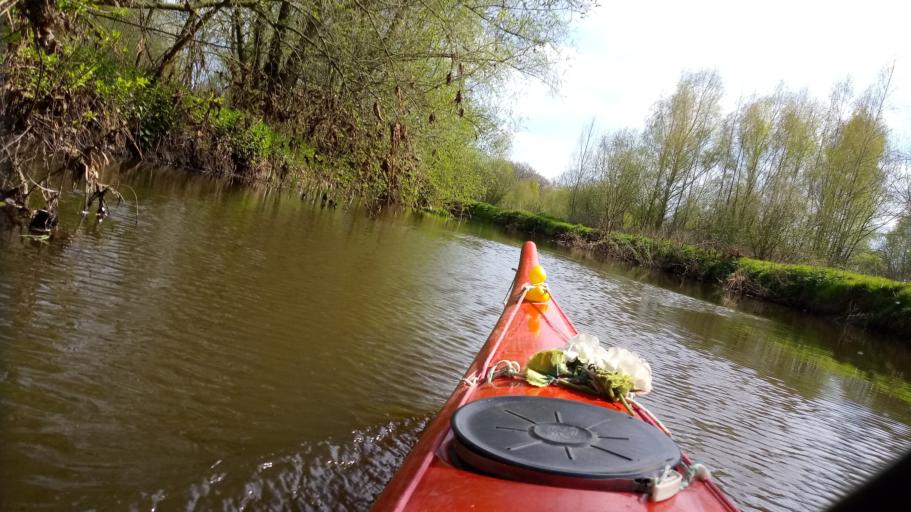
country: NL
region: Overijssel
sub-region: Gemeente Twenterand
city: Den Ham
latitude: 52.4400
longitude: 6.4404
